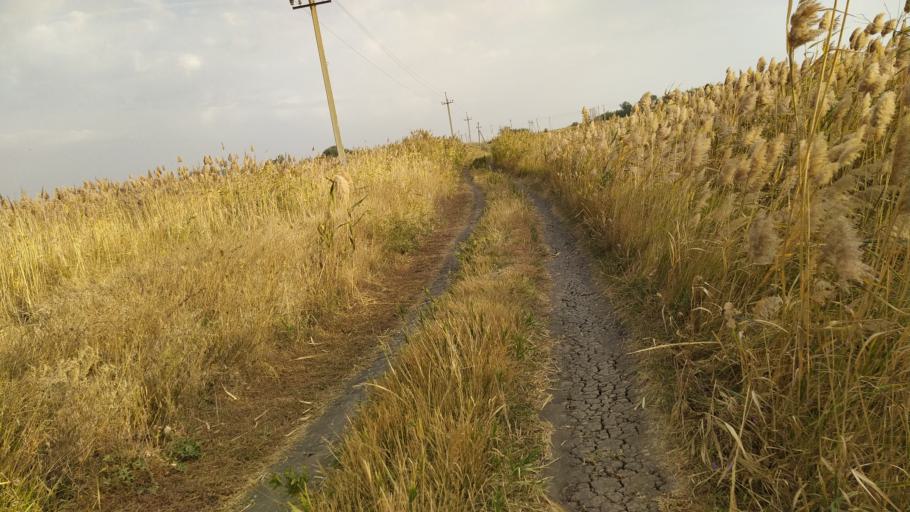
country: RU
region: Rostov
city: Kuleshovka
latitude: 47.1112
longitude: 39.6105
